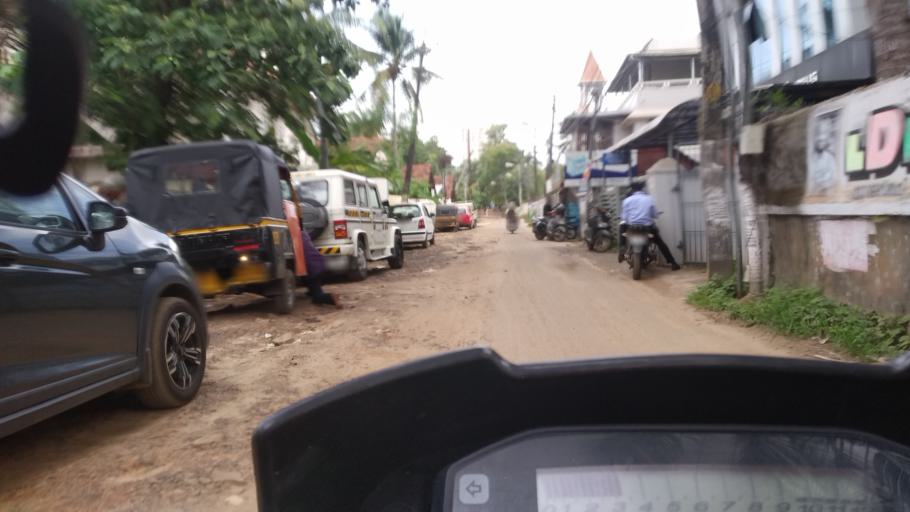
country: IN
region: Kerala
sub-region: Ernakulam
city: Cochin
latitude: 9.9875
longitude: 76.2945
